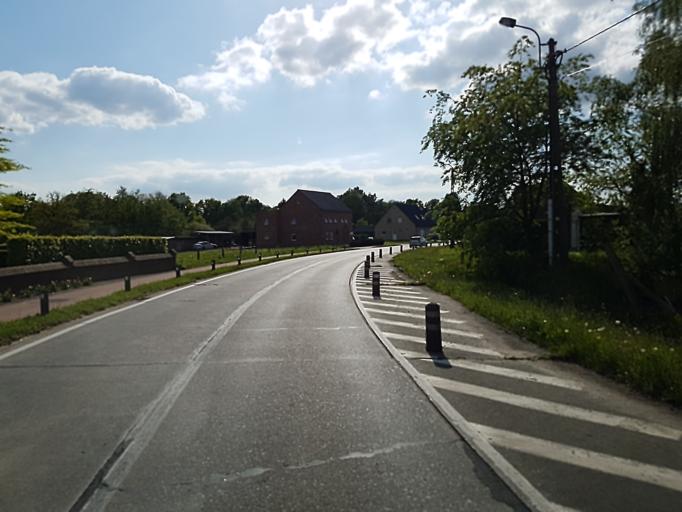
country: BE
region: Flanders
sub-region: Provincie Vlaams-Brabant
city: Begijnendijk
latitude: 51.0246
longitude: 4.7527
